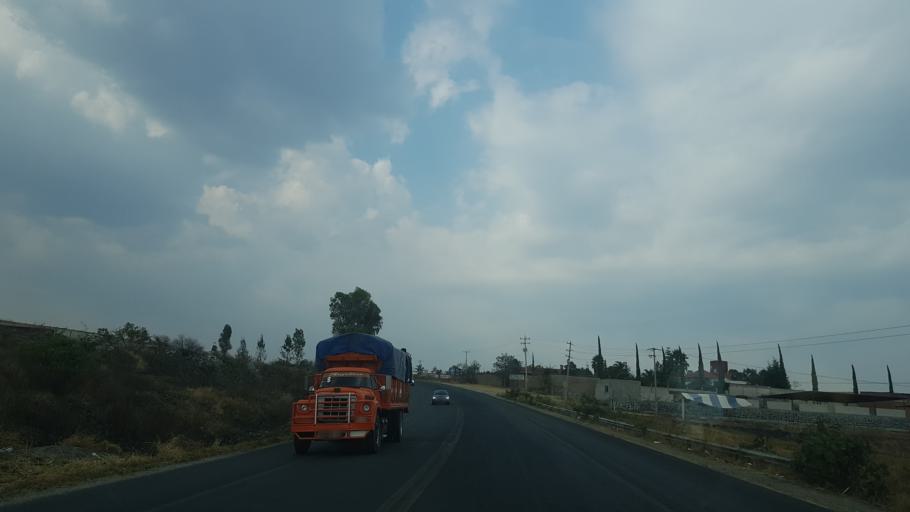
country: MX
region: Puebla
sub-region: Santa Isabel Cholula
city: Santa Ana Acozautla
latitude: 18.9682
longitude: -98.3825
